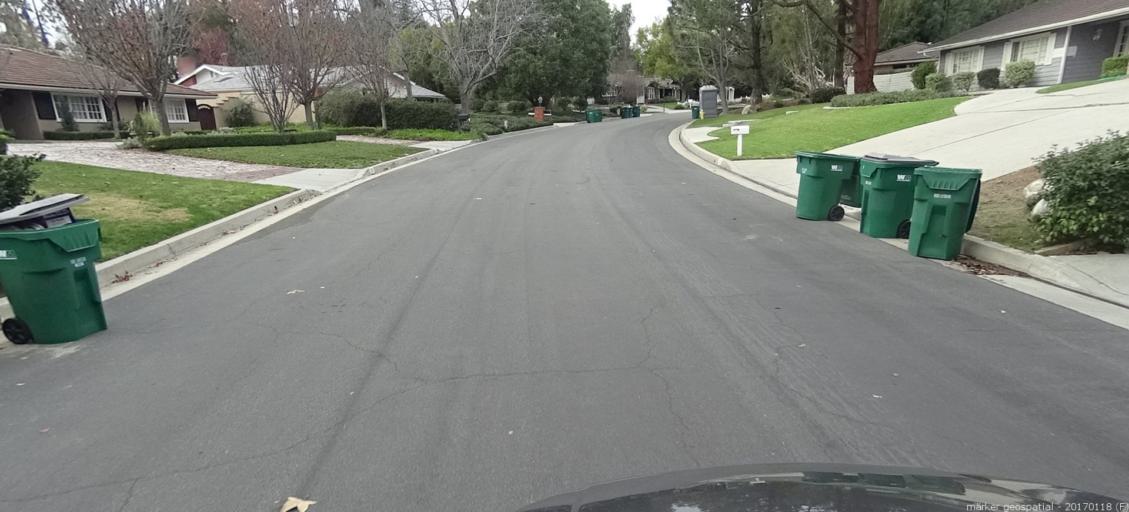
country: US
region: California
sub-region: Orange County
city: North Tustin
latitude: 33.7522
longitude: -117.7803
